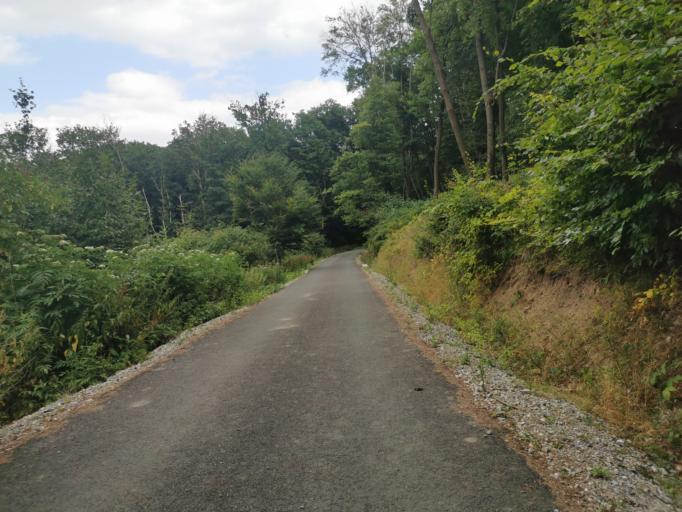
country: SK
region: Trenciansky
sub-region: Okres Myjava
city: Myjava
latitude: 48.7287
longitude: 17.5118
